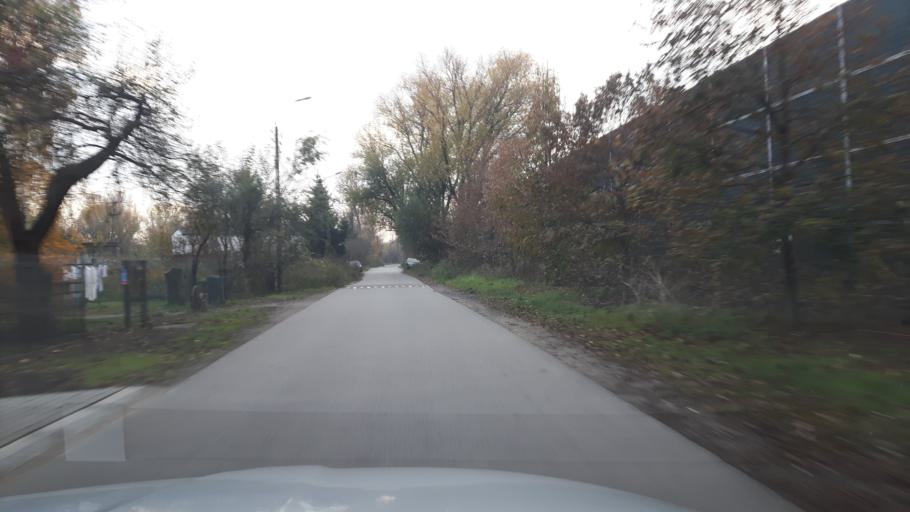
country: PL
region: Masovian Voivodeship
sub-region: Warszawa
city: Wilanow
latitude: 52.1879
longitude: 21.0958
